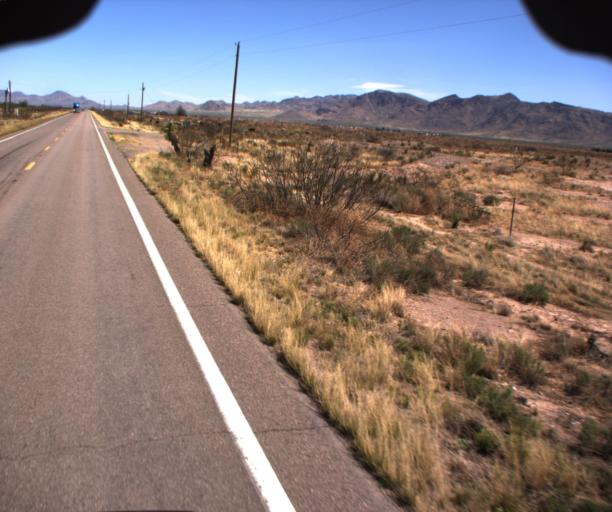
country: US
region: Arizona
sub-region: Cochise County
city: Douglas
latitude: 31.7878
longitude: -109.0652
